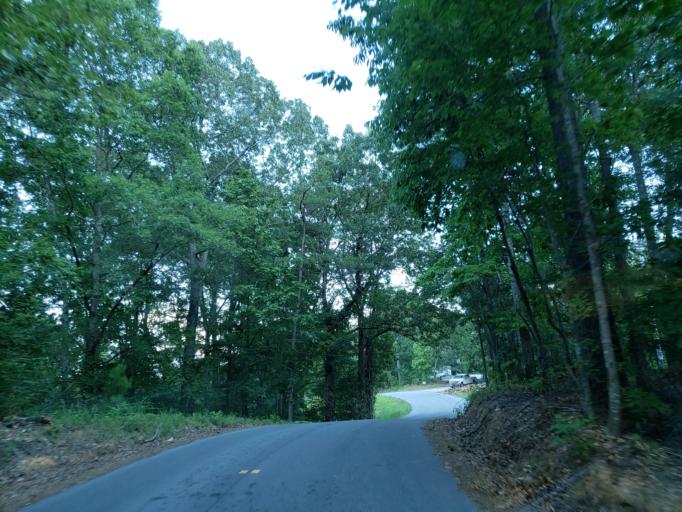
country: US
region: Georgia
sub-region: Paulding County
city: Dallas
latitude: 34.0188
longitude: -84.9026
